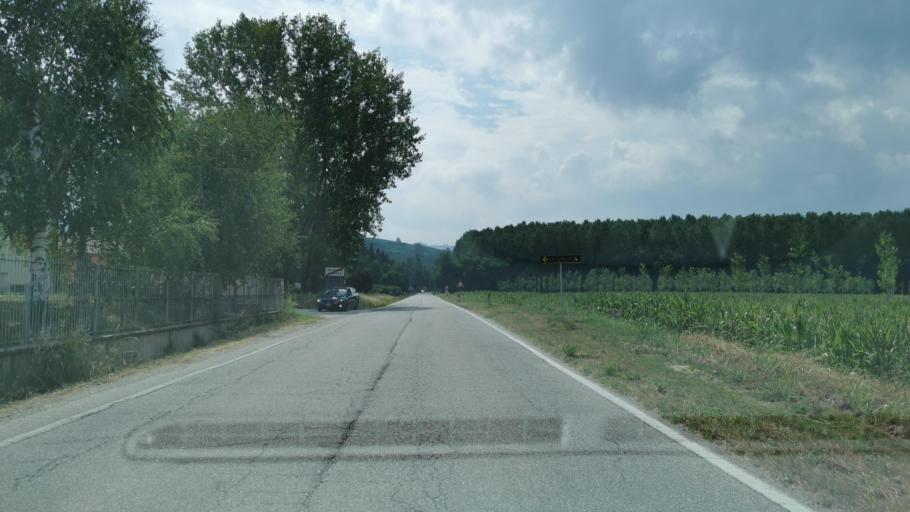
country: IT
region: Piedmont
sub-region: Provincia di Cuneo
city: Grinzane Cavour
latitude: 44.6511
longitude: 7.9911
